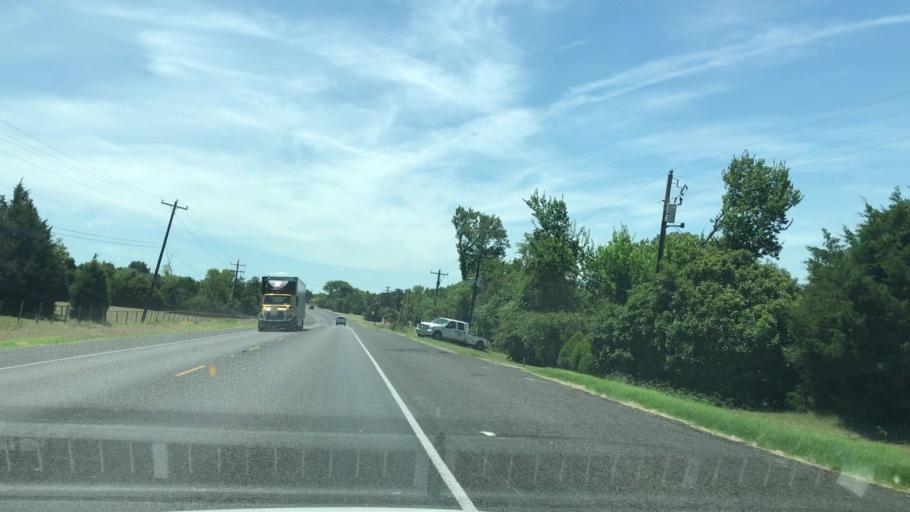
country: US
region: Texas
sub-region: Collin County
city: Lavon
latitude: 33.0002
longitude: -96.4642
